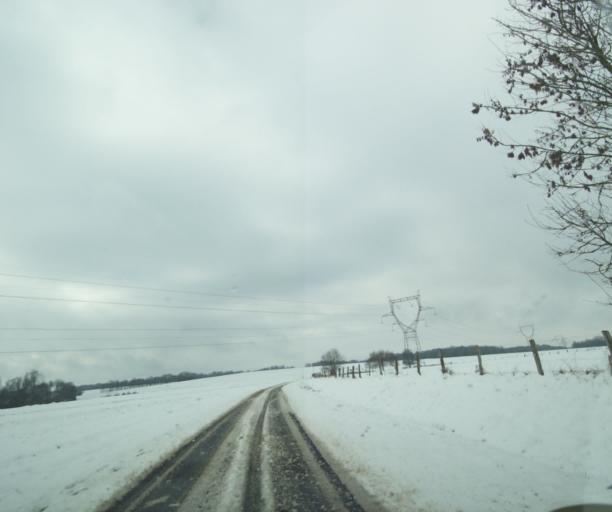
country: FR
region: Champagne-Ardenne
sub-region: Departement de la Haute-Marne
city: Montier-en-Der
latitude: 48.5092
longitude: 4.6909
